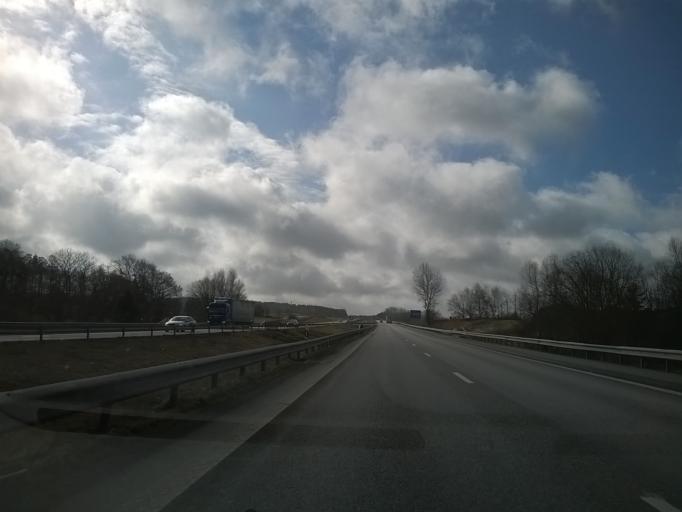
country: SE
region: Halland
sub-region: Kungsbacka Kommun
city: Frillesas
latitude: 57.2605
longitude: 12.2160
